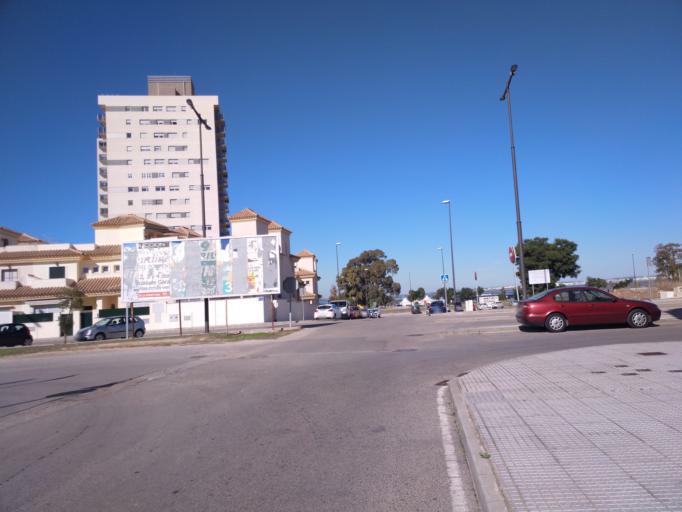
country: ES
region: Andalusia
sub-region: Provincia de Cadiz
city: San Fernando
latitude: 36.4824
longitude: -6.1984
